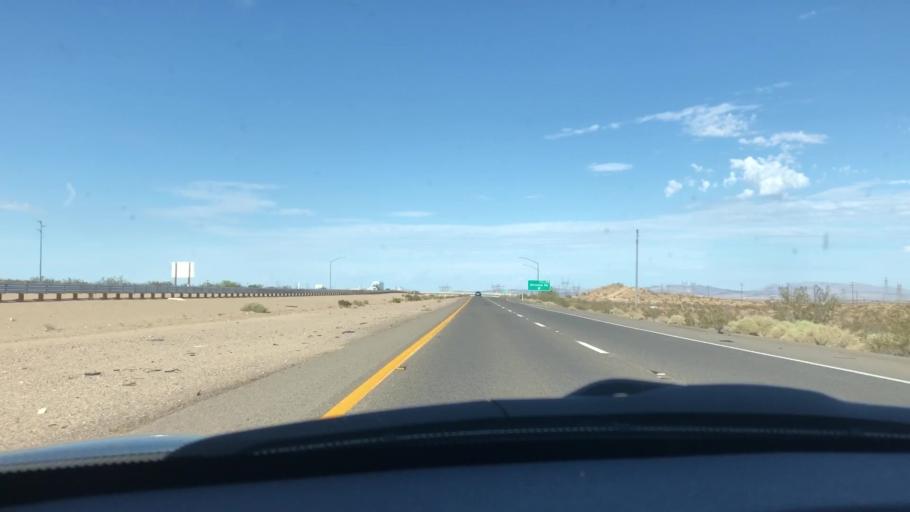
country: US
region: California
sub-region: San Bernardino County
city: Barstow
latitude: 34.9163
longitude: -116.7791
